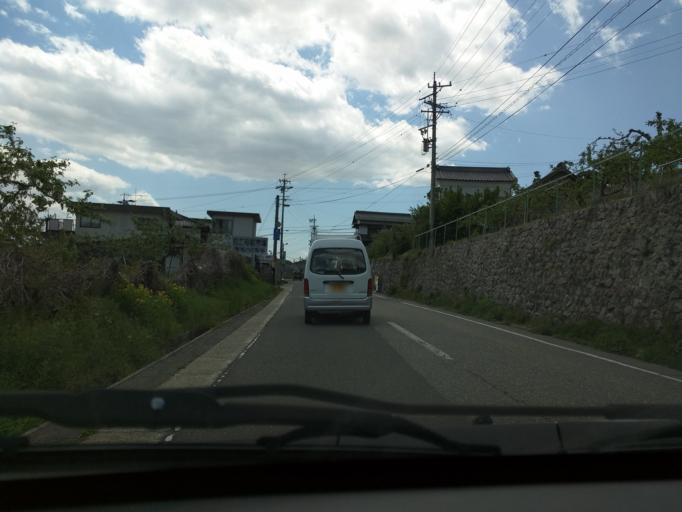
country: JP
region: Nagano
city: Nagano-shi
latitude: 36.6654
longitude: 138.1796
